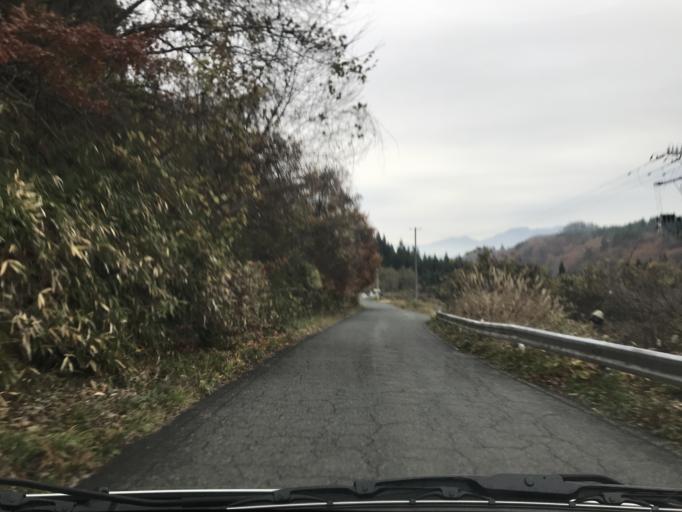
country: JP
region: Iwate
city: Ichinoseki
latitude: 39.0109
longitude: 141.0644
